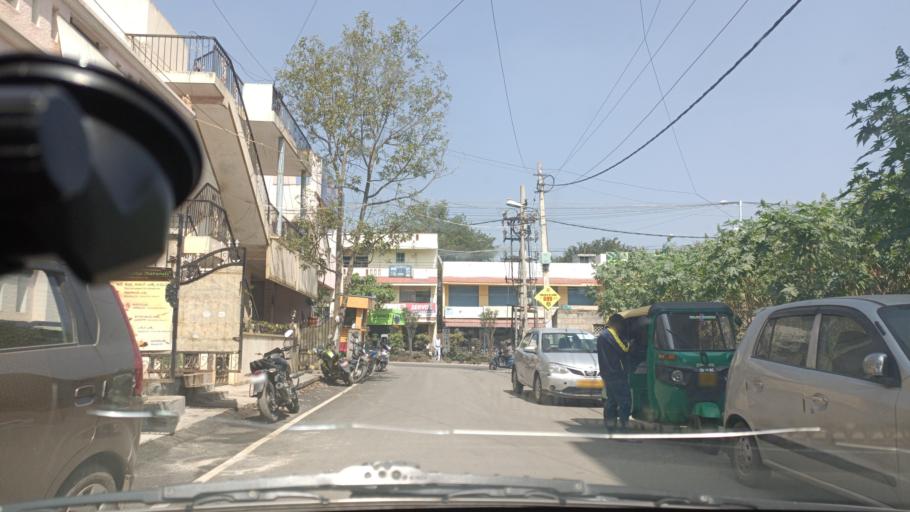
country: IN
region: Karnataka
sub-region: Bangalore Urban
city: Yelahanka
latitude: 13.1210
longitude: 77.6148
